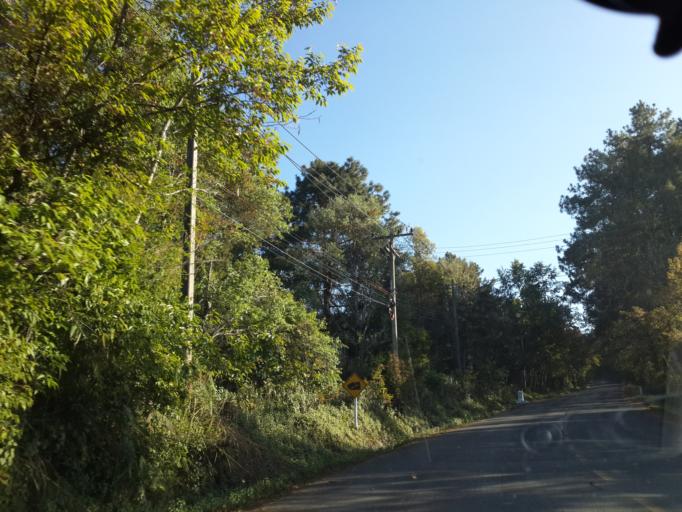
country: TH
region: Chiang Mai
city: Fang
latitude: 19.8885
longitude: 99.0466
